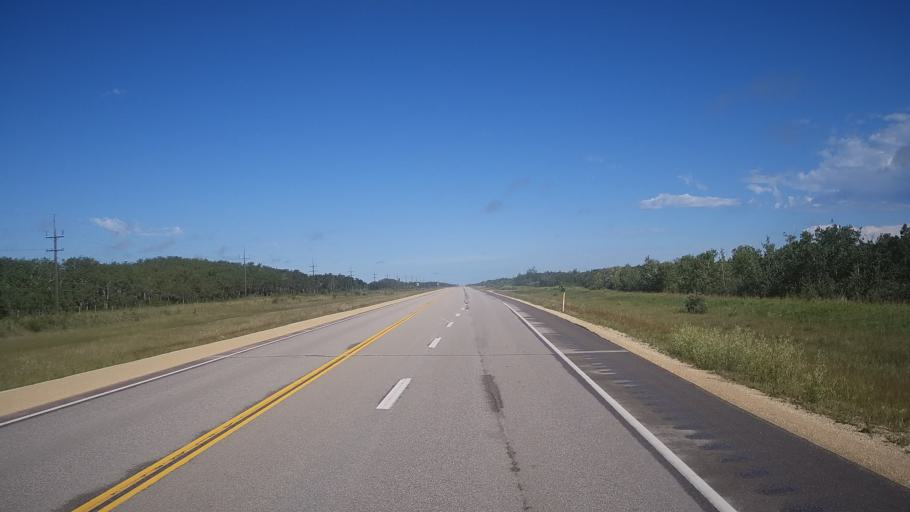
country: CA
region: Manitoba
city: Stonewall
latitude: 50.2212
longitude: -97.6839
